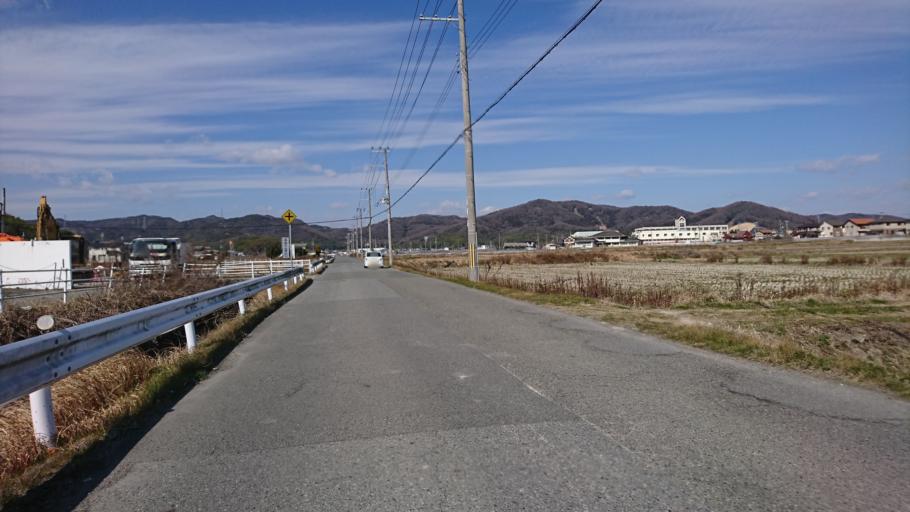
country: JP
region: Hyogo
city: Kakogawacho-honmachi
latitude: 34.8119
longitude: 134.8076
